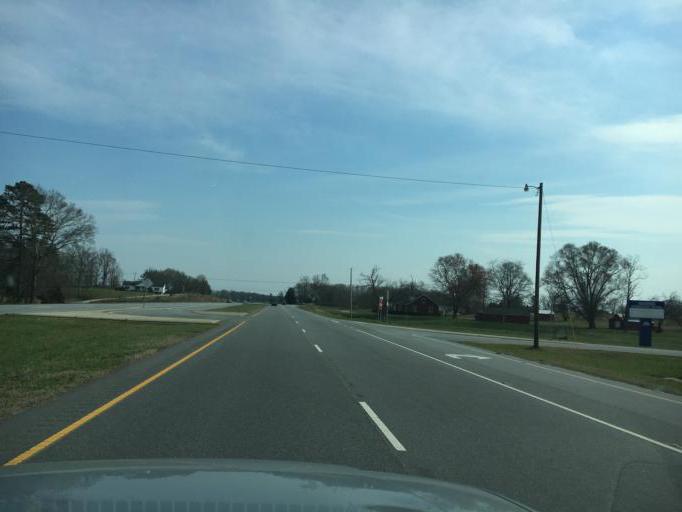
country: US
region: North Carolina
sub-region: Rutherford County
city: Forest City
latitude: 35.2756
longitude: -81.8950
